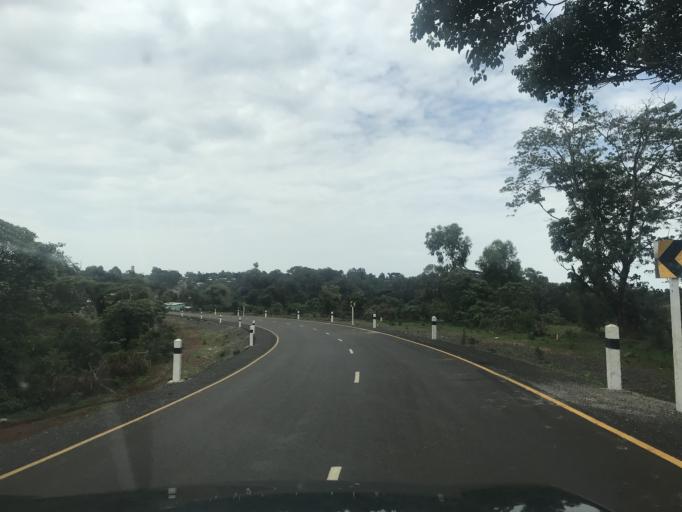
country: ET
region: Oromiya
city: Shambu
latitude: 9.8721
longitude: 36.6766
